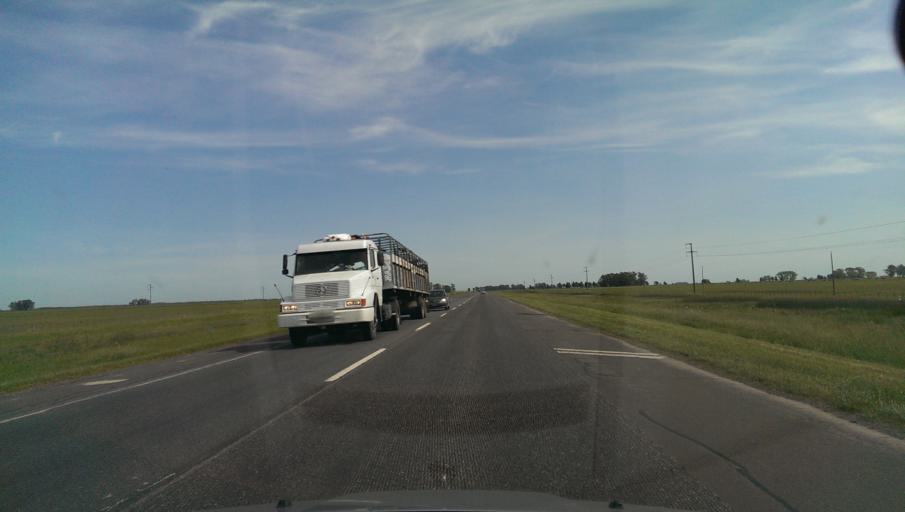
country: AR
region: Buenos Aires
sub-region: Partido de Azul
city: Azul
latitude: -36.4135
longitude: -59.5182
